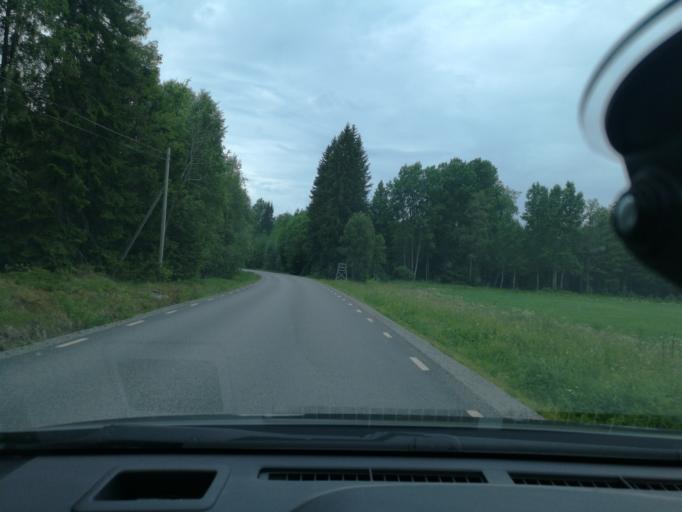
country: SE
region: Vaestmanland
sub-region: Vasteras
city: Skultuna
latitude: 59.7932
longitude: 16.3635
